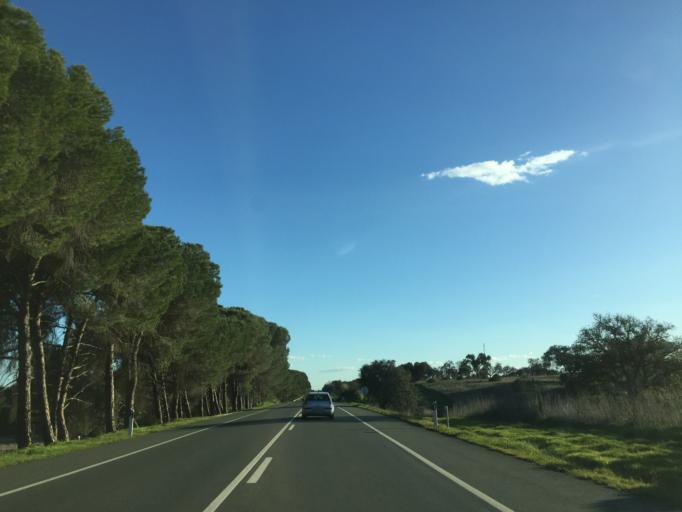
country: PT
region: Setubal
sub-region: Grandola
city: Grandola
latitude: 38.0851
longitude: -8.4176
